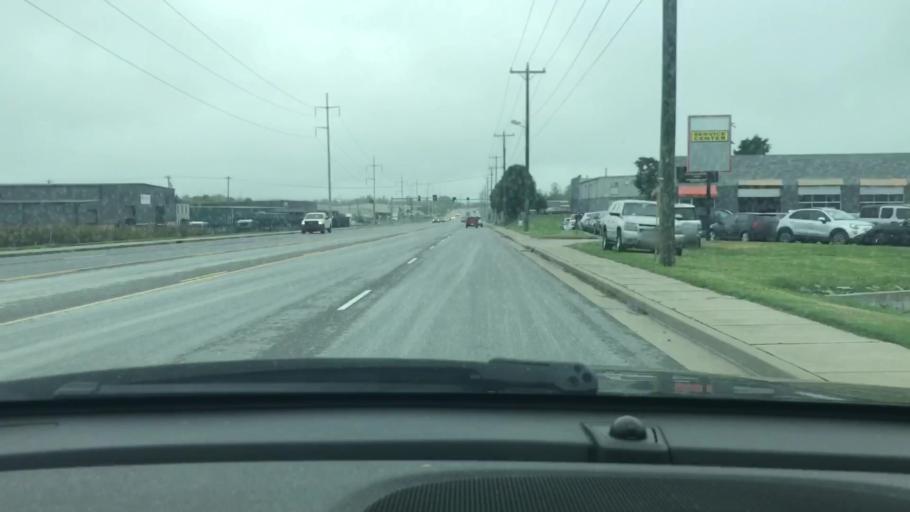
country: US
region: Tennessee
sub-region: Rutherford County
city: La Vergne
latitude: 36.0129
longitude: -86.5938
